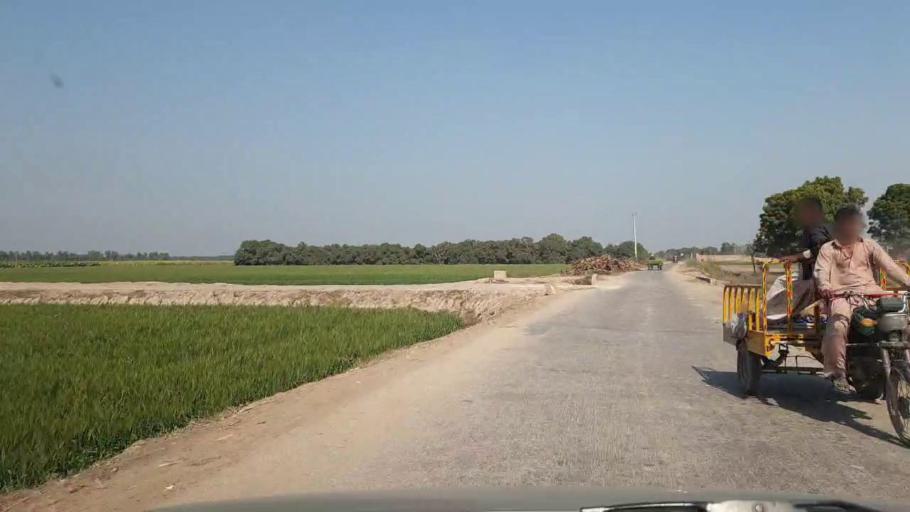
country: PK
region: Sindh
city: Tando Allahyar
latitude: 25.4374
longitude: 68.6526
